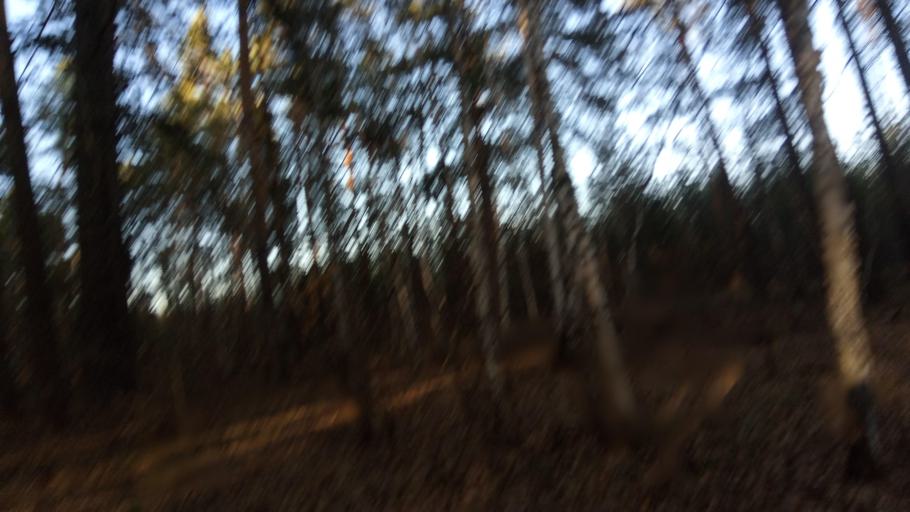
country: RU
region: Chelyabinsk
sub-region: Gorod Chelyabinsk
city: Chelyabinsk
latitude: 55.1386
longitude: 61.3365
